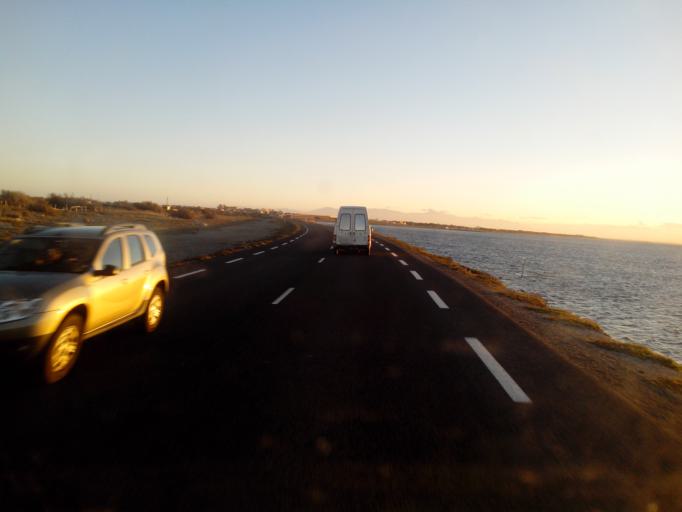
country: FR
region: Languedoc-Roussillon
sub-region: Departement de l'Aude
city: Leucate
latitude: 42.8947
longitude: 3.0479
